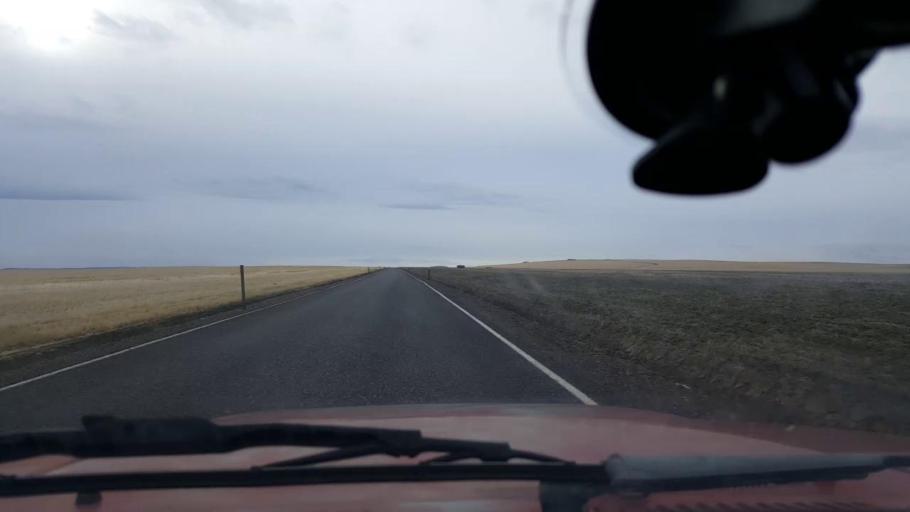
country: US
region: Washington
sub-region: Asotin County
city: Clarkston Heights-Vineland
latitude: 46.3525
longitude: -117.2294
